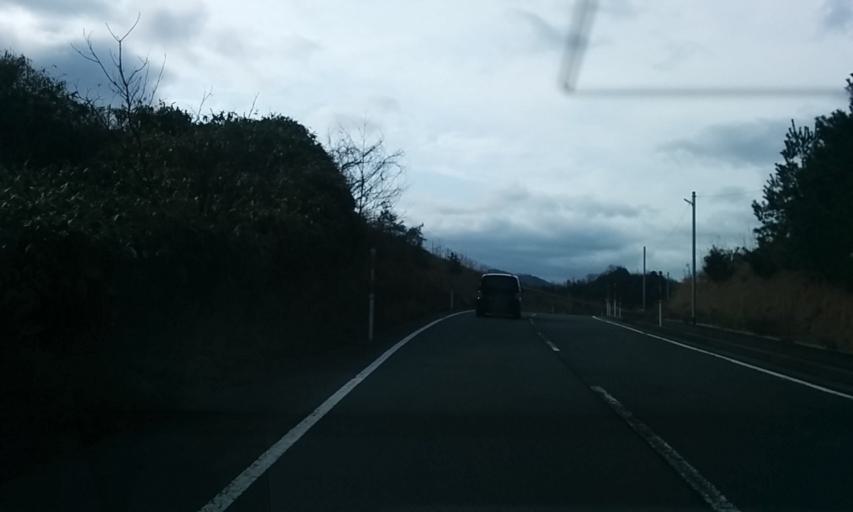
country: JP
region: Kyoto
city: Miyazu
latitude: 35.5828
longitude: 135.1054
